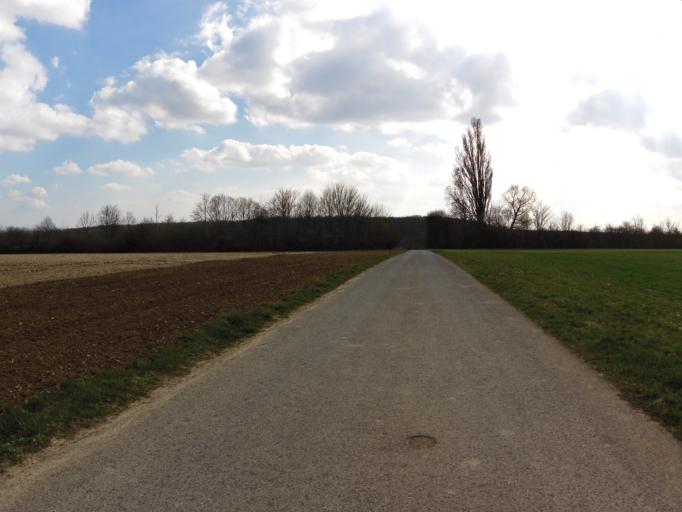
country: DE
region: Bavaria
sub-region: Regierungsbezirk Unterfranken
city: Buchbrunn
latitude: 49.7389
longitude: 10.1117
